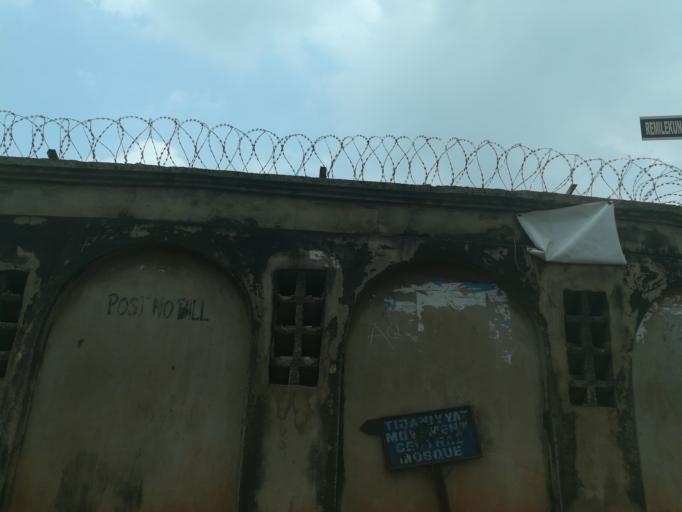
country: NG
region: Lagos
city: Ikorodu
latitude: 6.6190
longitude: 3.5196
